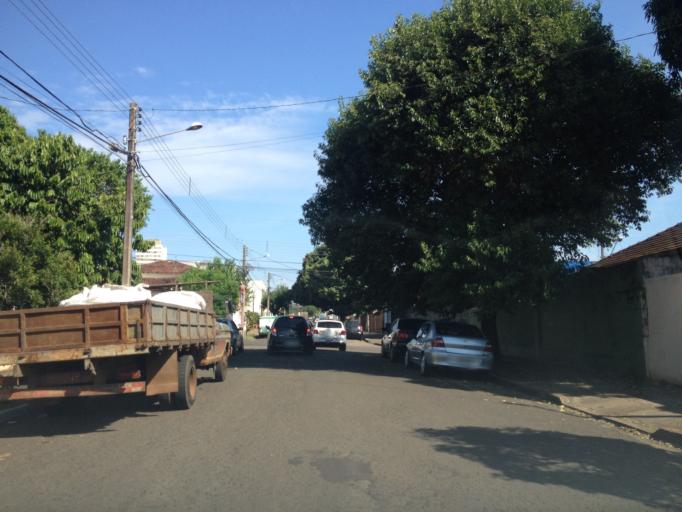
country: BR
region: Parana
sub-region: Londrina
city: Londrina
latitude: -23.2991
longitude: -51.1611
